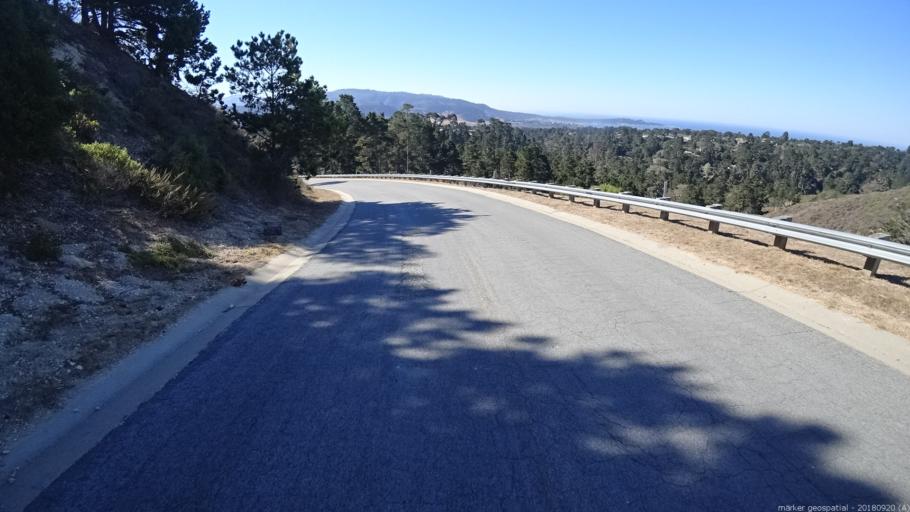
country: US
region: California
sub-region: Monterey County
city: Carmel-by-the-Sea
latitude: 36.5601
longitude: -121.9010
